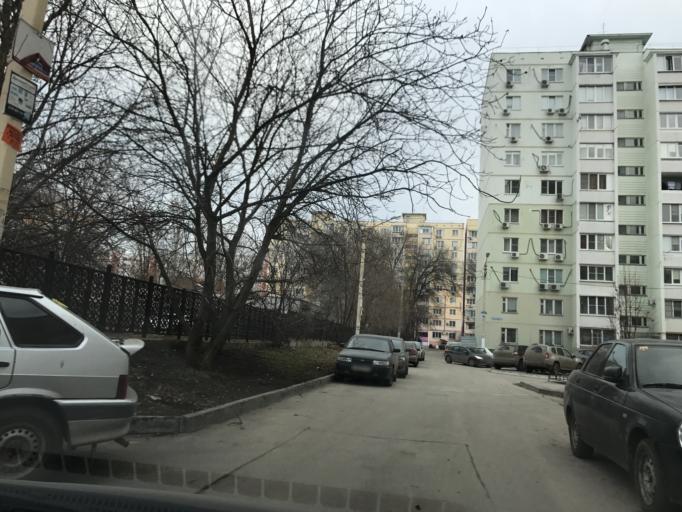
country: RU
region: Rostov
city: Rostov-na-Donu
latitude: 47.2227
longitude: 39.6233
